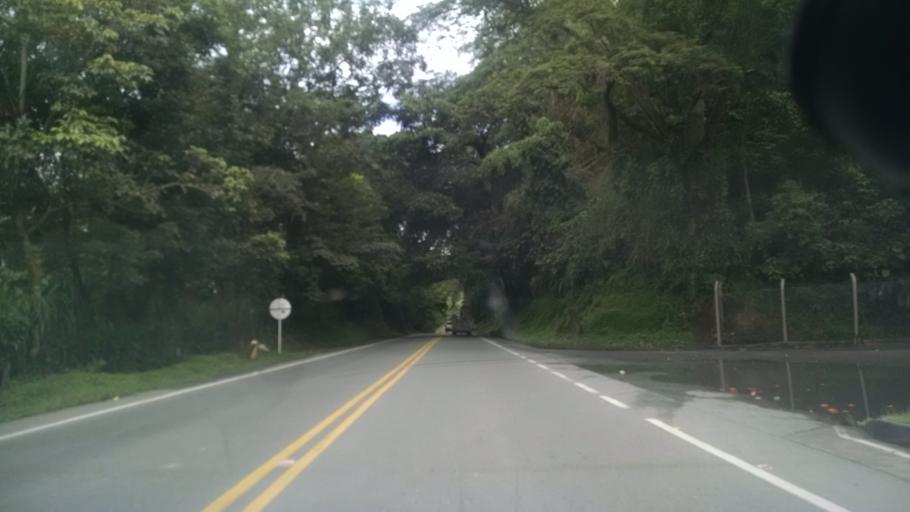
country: CO
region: Caldas
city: Palestina
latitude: 5.0604
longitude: -75.6095
